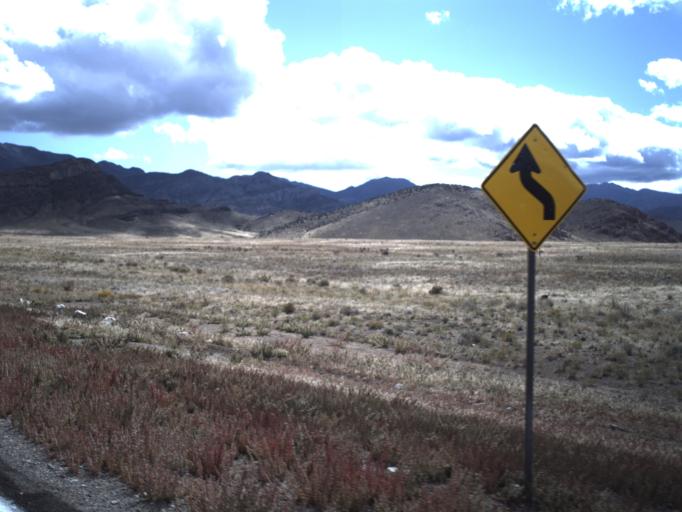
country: US
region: Utah
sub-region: Beaver County
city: Milford
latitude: 38.5078
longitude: -113.6155
